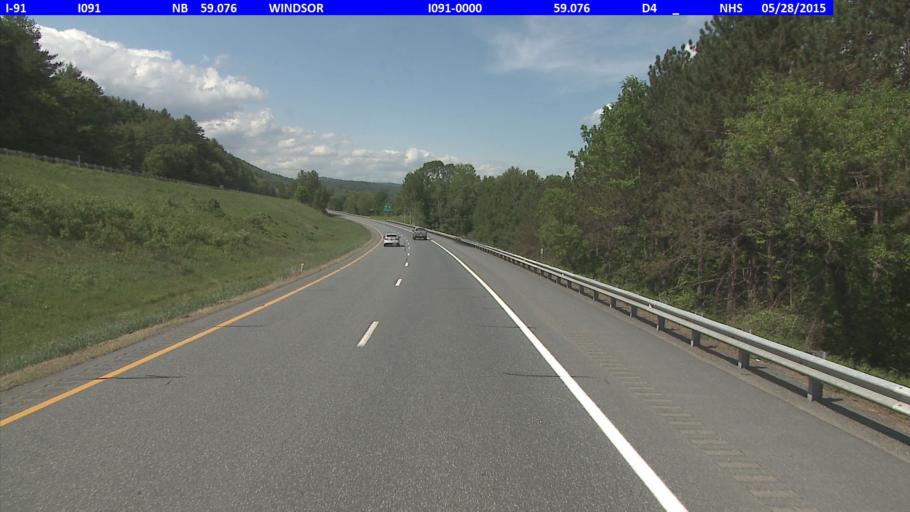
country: US
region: Vermont
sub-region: Windsor County
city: Windsor
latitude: 43.5096
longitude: -72.4059
